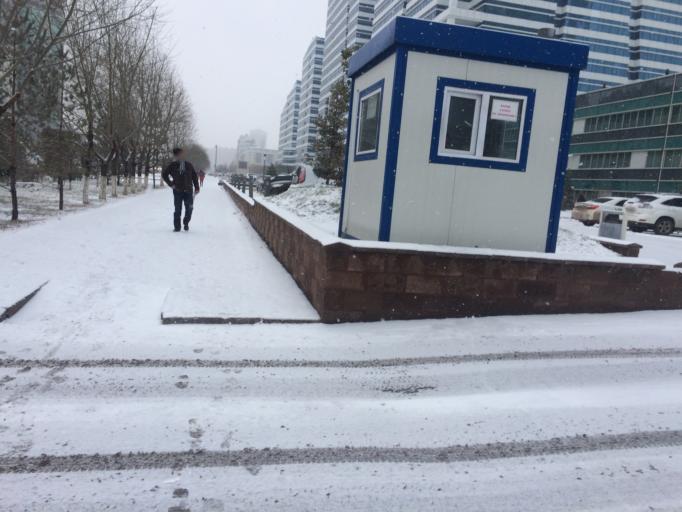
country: KZ
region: Astana Qalasy
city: Astana
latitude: 51.1314
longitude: 71.4247
